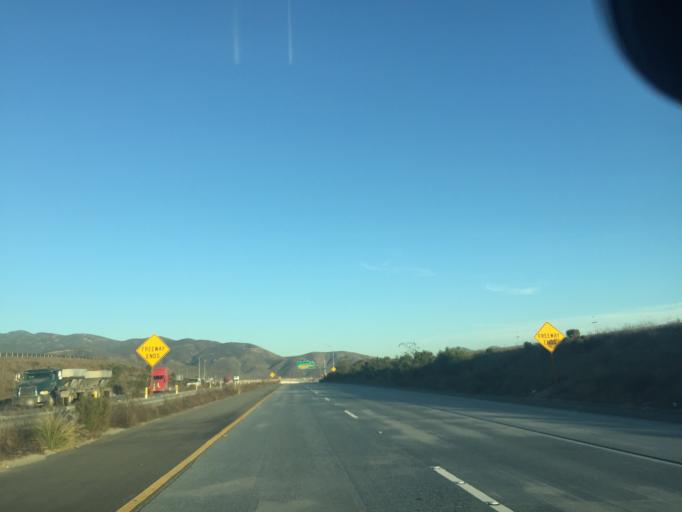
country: MX
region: Baja California
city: Tijuana
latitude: 32.5639
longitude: -116.9348
